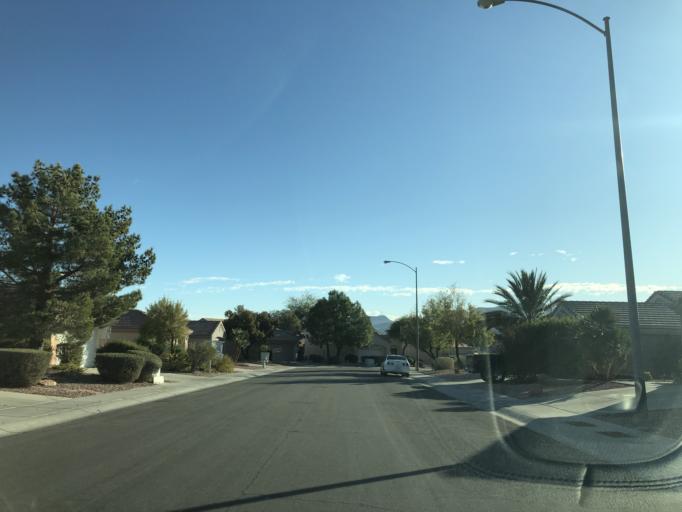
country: US
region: Nevada
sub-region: Clark County
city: Whitney
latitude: 36.0119
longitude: -115.0767
